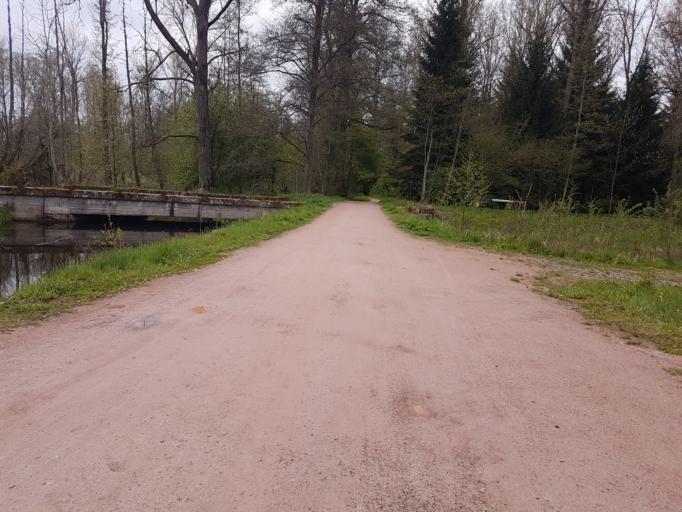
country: DE
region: Baden-Wuerttemberg
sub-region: Freiburg Region
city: Donaueschingen
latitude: 47.9457
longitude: 8.5073
